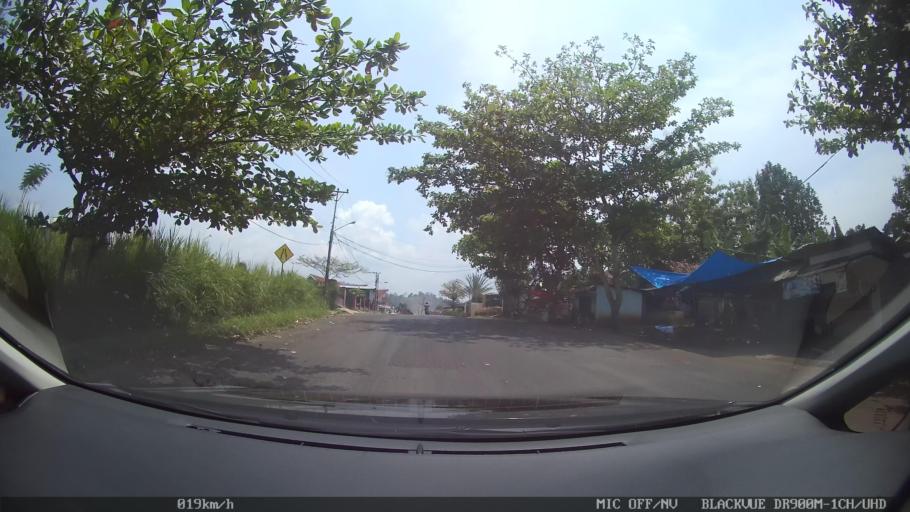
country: ID
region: Lampung
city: Bandarlampung
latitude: -5.4382
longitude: 105.2413
